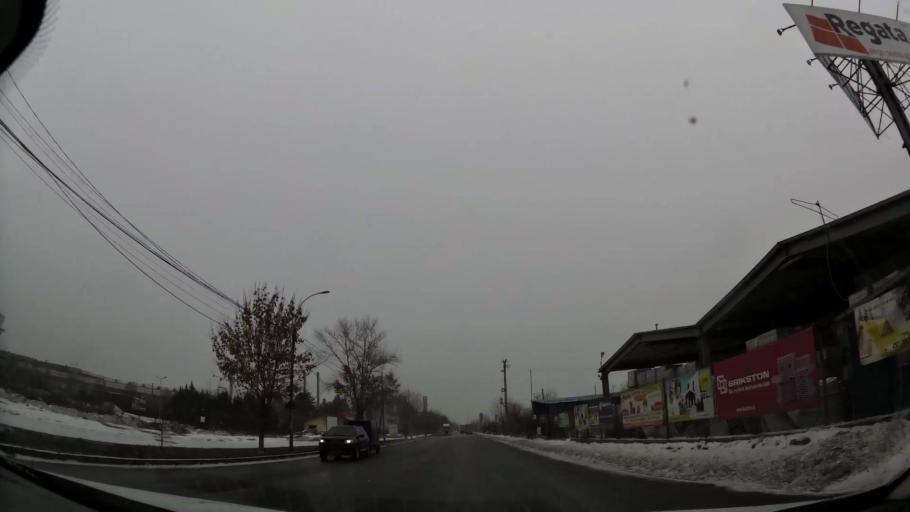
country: RO
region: Dambovita
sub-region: Municipiul Targoviste
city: Targoviste
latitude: 44.9179
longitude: 25.4382
